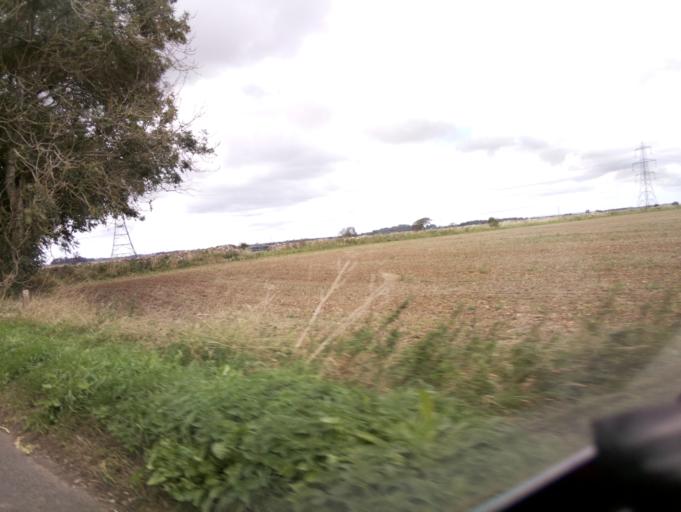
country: GB
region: England
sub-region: South Gloucestershire
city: Marshfield
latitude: 51.4942
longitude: -2.3189
